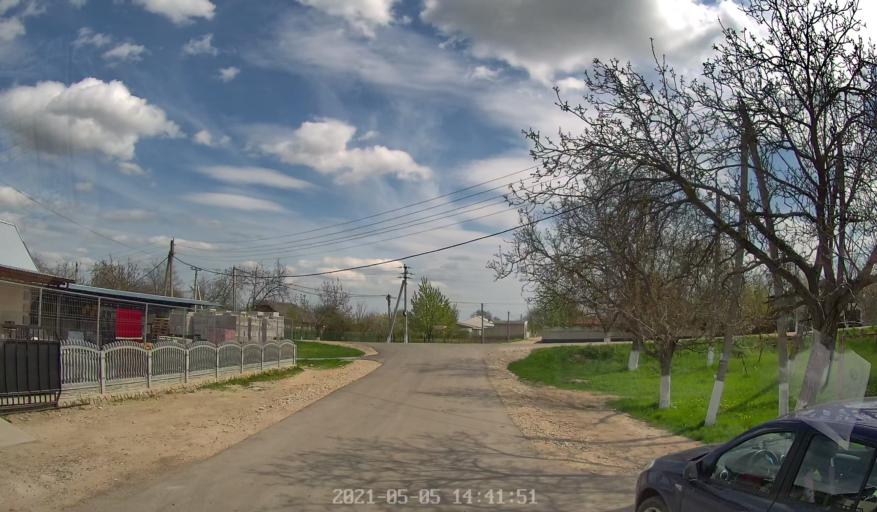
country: MD
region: Chisinau
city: Vadul lui Voda
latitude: 47.0912
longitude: 29.1720
